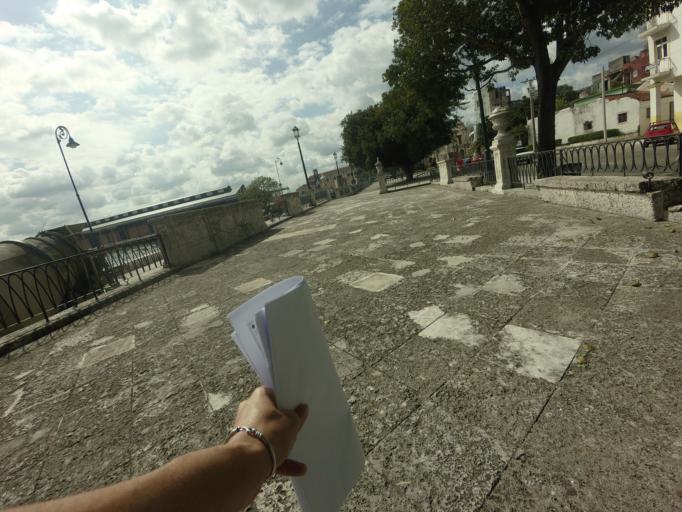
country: CU
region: La Habana
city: La Habana Vieja
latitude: 23.1321
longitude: -82.3480
